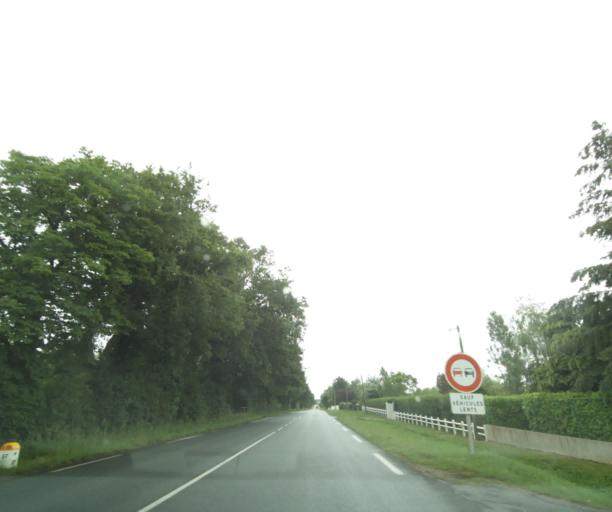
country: FR
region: Poitou-Charentes
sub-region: Departement des Deux-Sevres
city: Viennay
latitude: 46.6785
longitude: -0.2450
